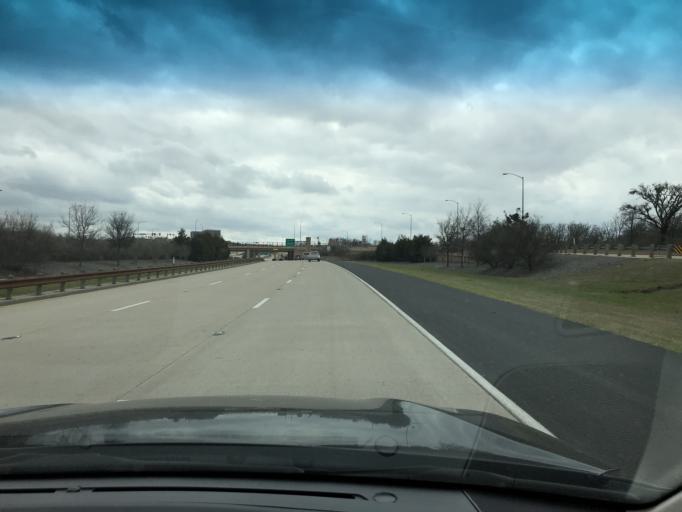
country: US
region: Texas
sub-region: Tarrant County
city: Westworth
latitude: 32.7014
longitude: -97.4064
